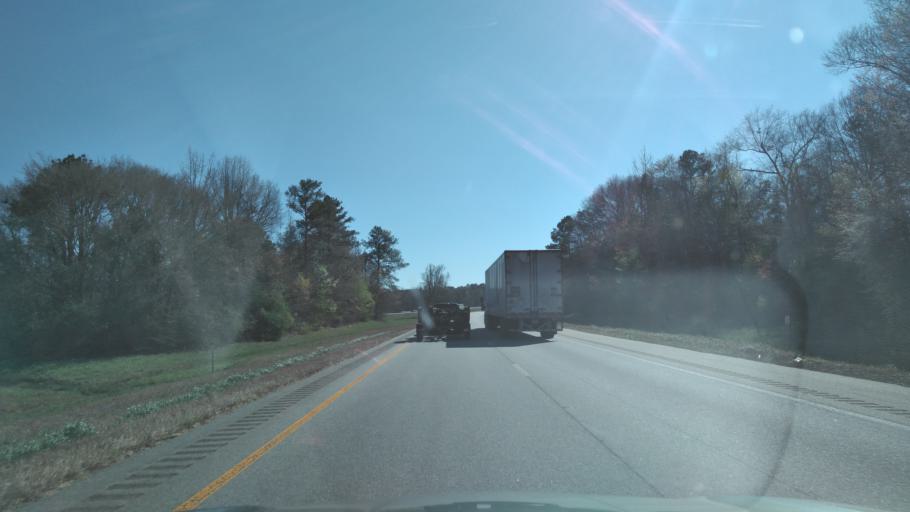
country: US
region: Alabama
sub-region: Lowndes County
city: Fort Deposit
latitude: 31.9676
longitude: -86.5372
